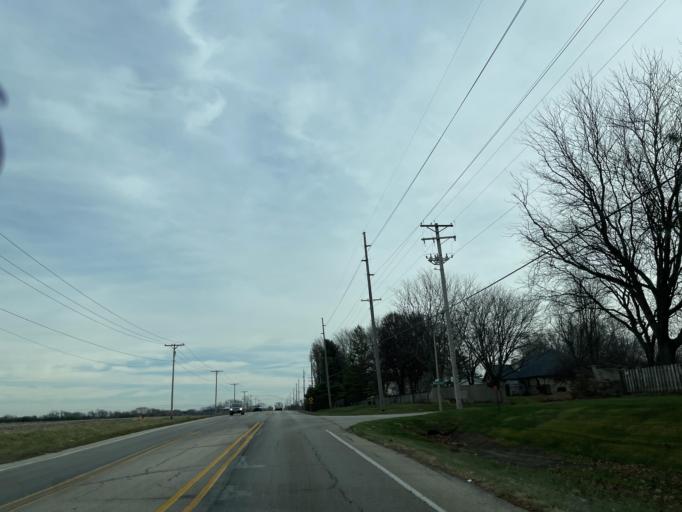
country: US
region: Illinois
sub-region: Sangamon County
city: Leland Grove
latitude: 39.7867
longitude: -89.7294
